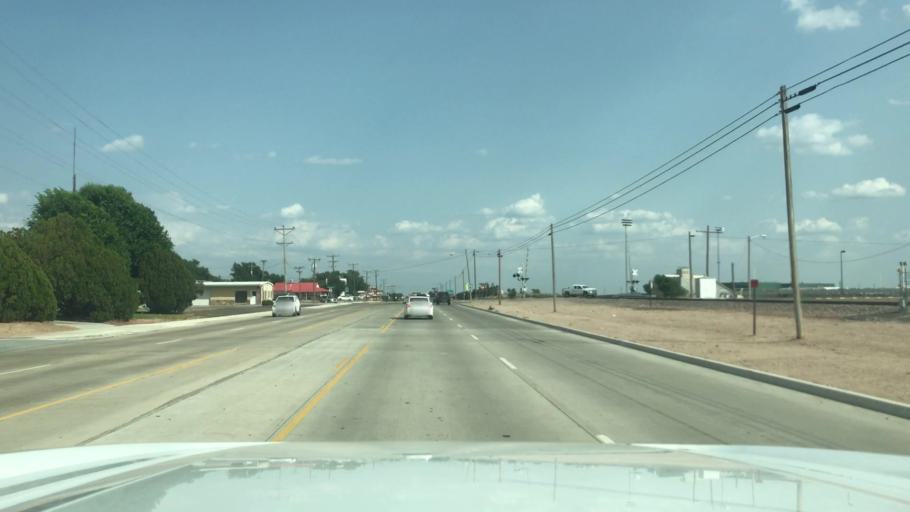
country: US
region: Texas
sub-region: Dallam County
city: Dalhart
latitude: 36.0518
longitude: -102.5021
